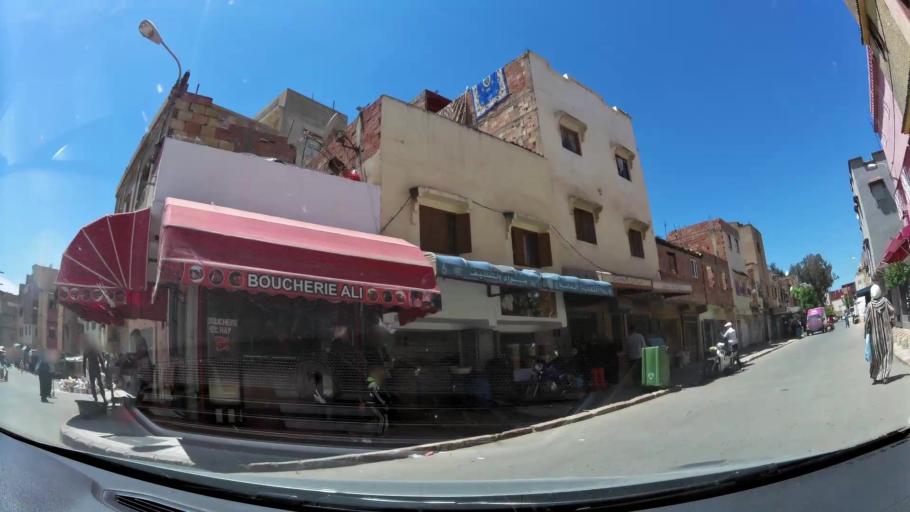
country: MA
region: Meknes-Tafilalet
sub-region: Meknes
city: Meknes
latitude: 33.9094
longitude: -5.5785
